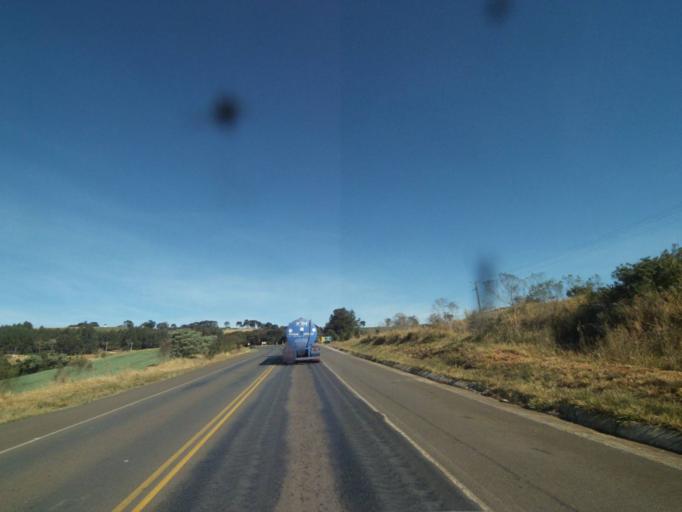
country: BR
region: Parana
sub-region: Tibagi
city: Tibagi
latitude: -24.4977
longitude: -50.4453
